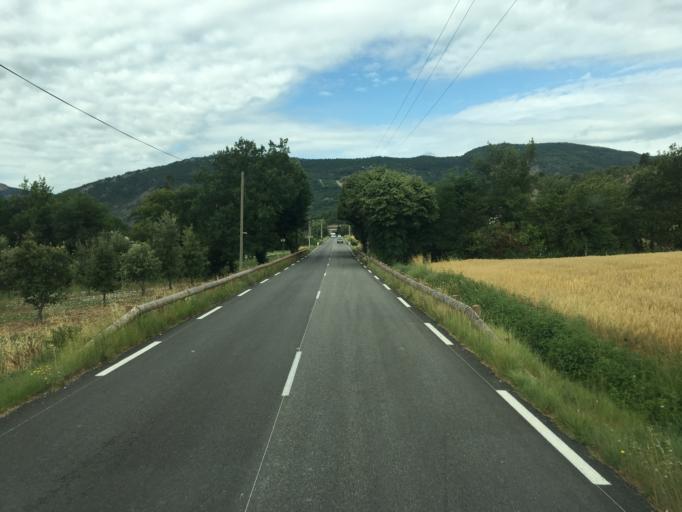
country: FR
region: Rhone-Alpes
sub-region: Departement de la Drome
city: Nyons
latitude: 44.3925
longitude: 5.2109
